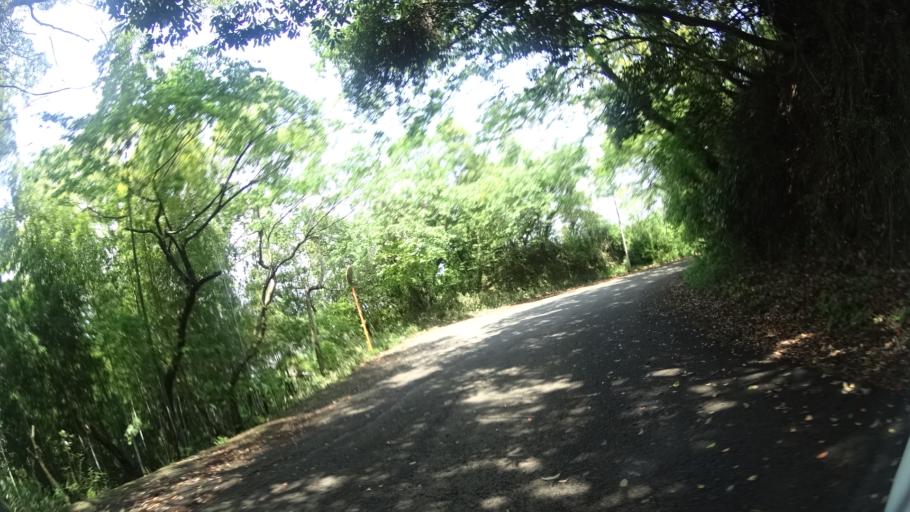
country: JP
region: Tokushima
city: Tokushima-shi
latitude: 34.0681
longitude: 134.5140
